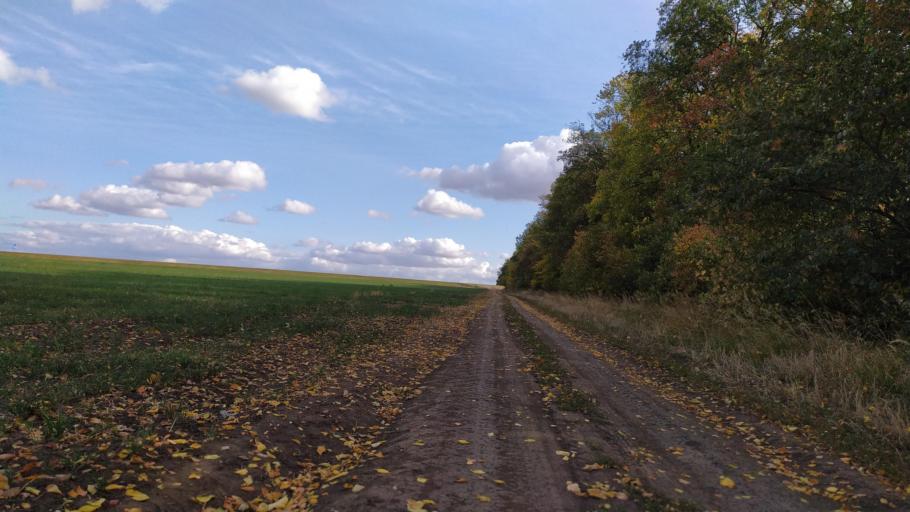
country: RU
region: Kursk
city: Kursk
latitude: 51.6183
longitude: 36.1633
